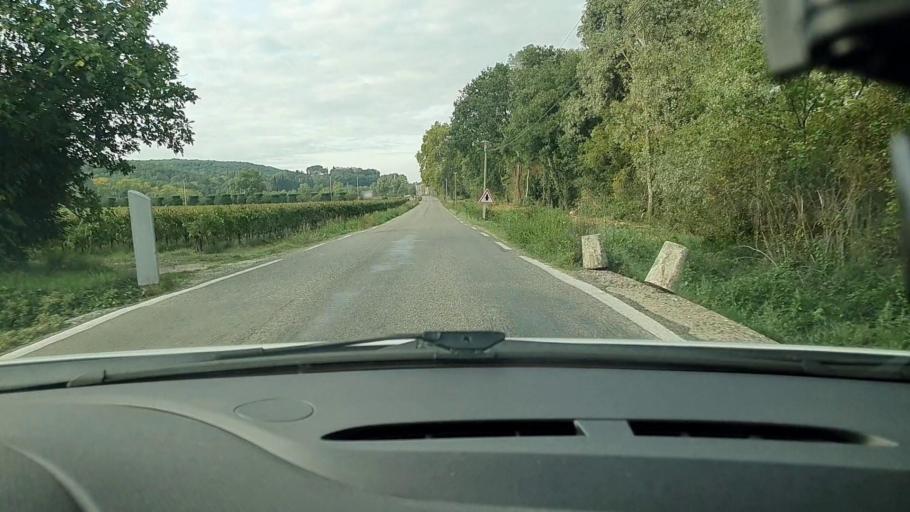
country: FR
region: Languedoc-Roussillon
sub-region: Departement du Gard
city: Saint-Ambroix
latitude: 44.2119
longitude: 4.2570
